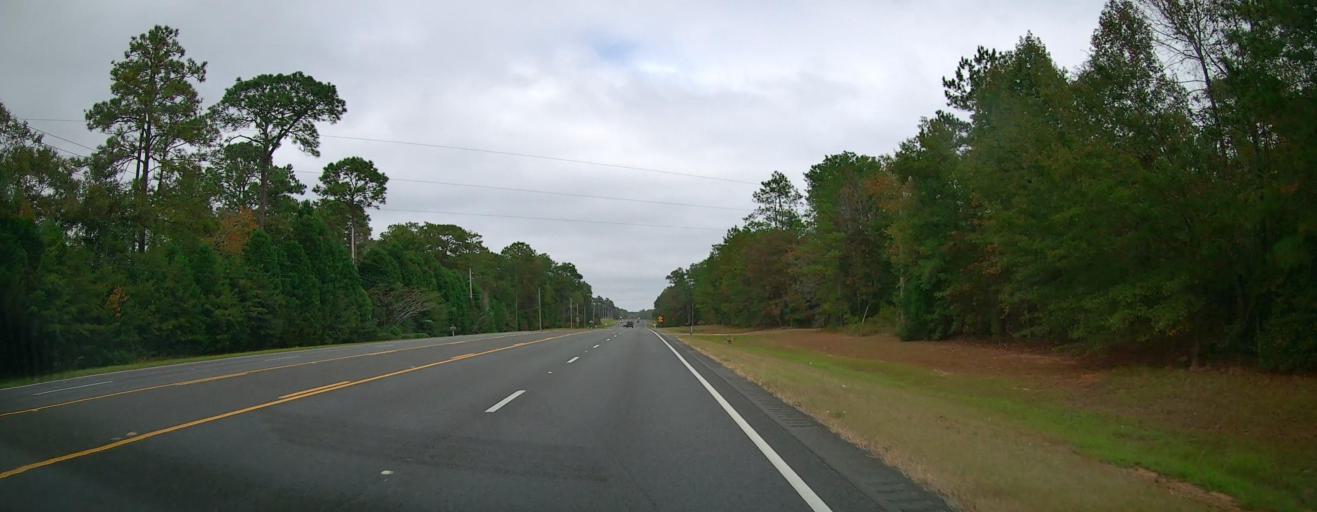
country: US
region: Georgia
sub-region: Thomas County
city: Thomasville
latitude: 30.9083
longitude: -83.9231
